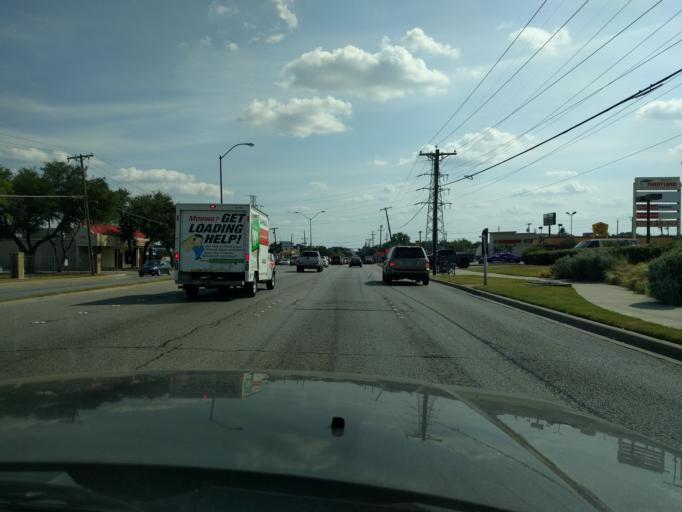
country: US
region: Texas
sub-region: Dallas County
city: Richardson
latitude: 32.9416
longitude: -96.7690
